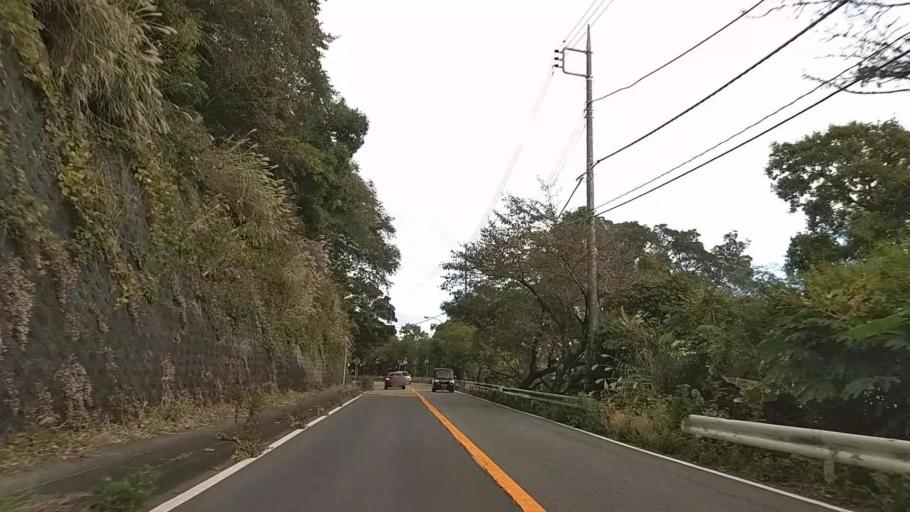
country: JP
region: Shizuoka
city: Atami
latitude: 35.1175
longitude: 139.0951
